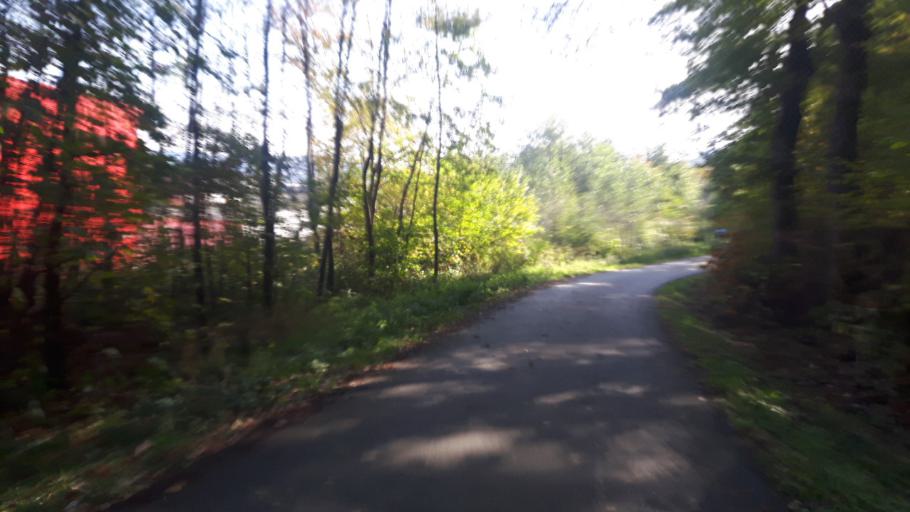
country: DE
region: North Rhine-Westphalia
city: Netphen
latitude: 50.8871
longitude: 8.1247
